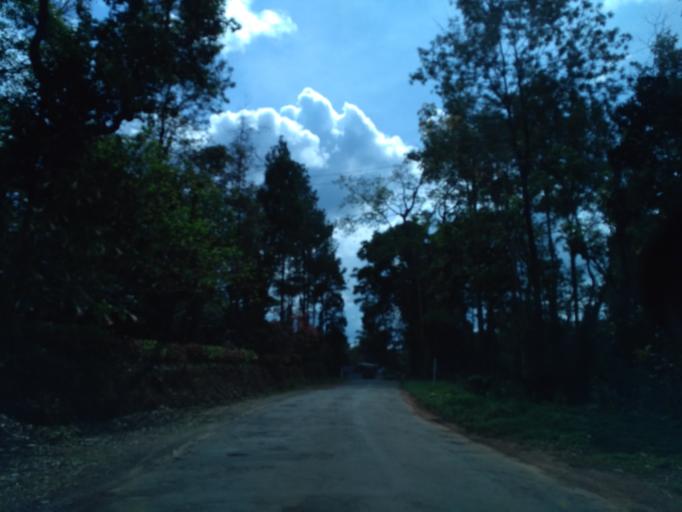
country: IN
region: Karnataka
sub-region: Kodagu
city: Madikeri
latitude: 12.3532
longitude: 75.6711
